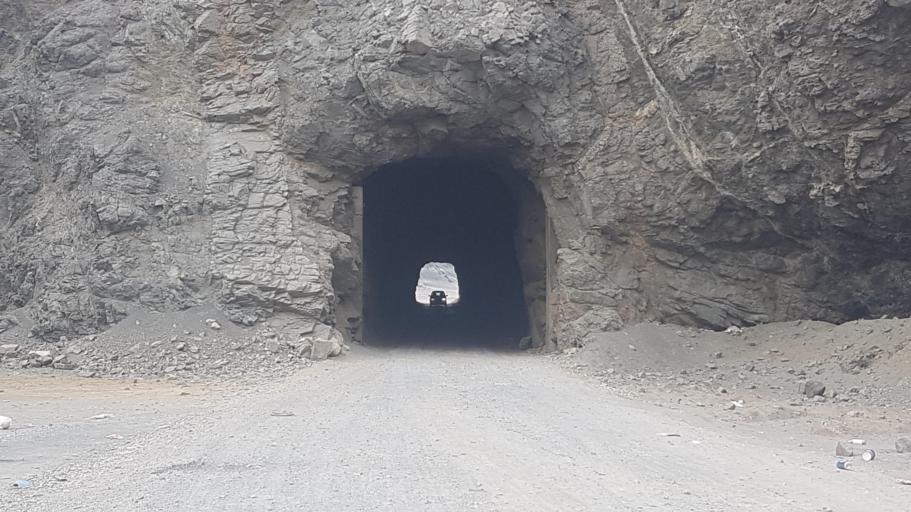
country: PE
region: Ancash
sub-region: Provincia de Santa
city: Samanco
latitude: -9.2064
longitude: -78.4850
